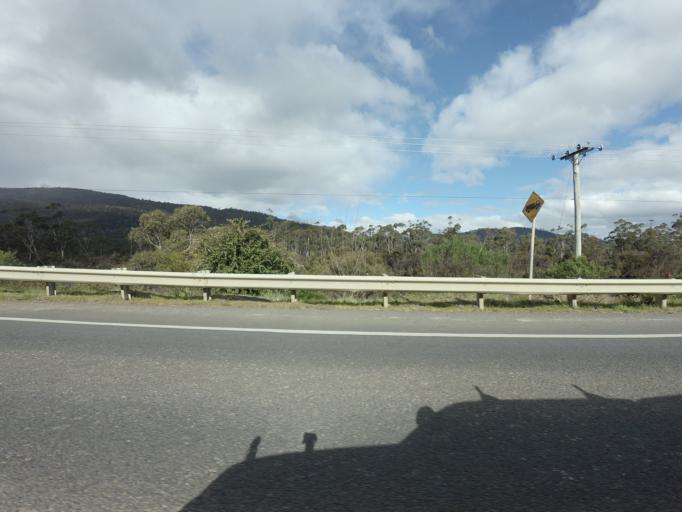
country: AU
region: Tasmania
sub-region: Huon Valley
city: Huonville
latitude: -43.0557
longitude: 147.0328
